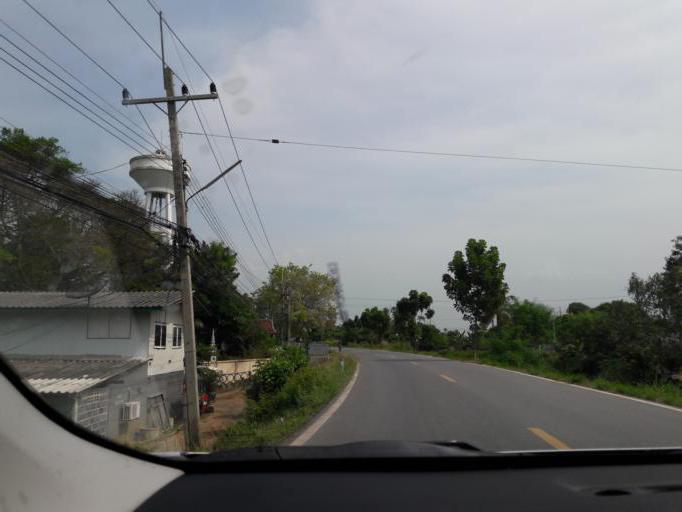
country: TH
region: Ang Thong
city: Ang Thong
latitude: 14.5883
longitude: 100.4682
